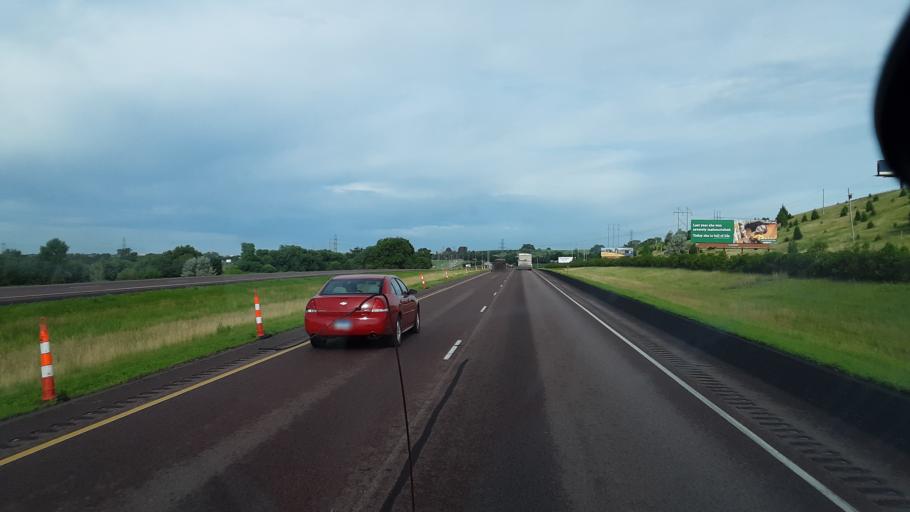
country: US
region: South Dakota
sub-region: Minnehaha County
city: Brandon
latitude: 43.6106
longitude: -96.6343
